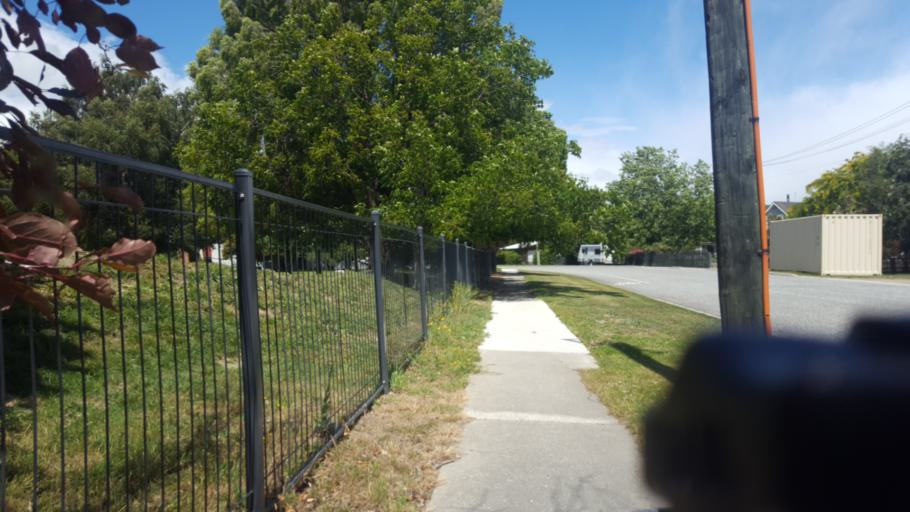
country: NZ
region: Otago
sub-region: Queenstown-Lakes District
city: Wanaka
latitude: -45.1909
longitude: 169.3180
